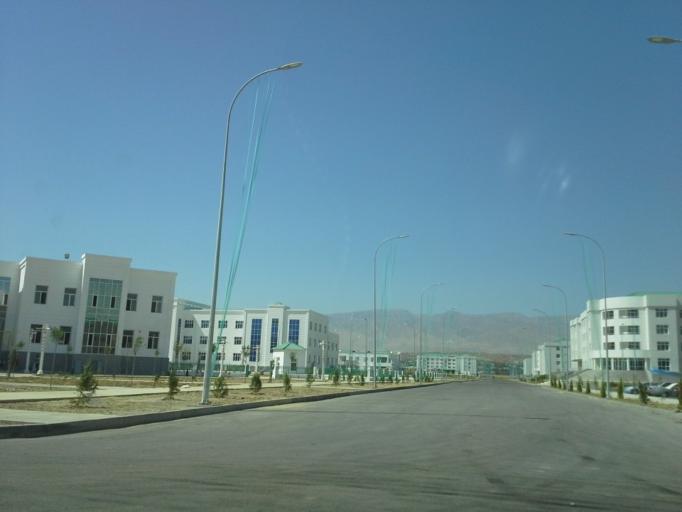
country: TM
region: Ahal
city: Ashgabat
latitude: 37.9787
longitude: 58.3284
